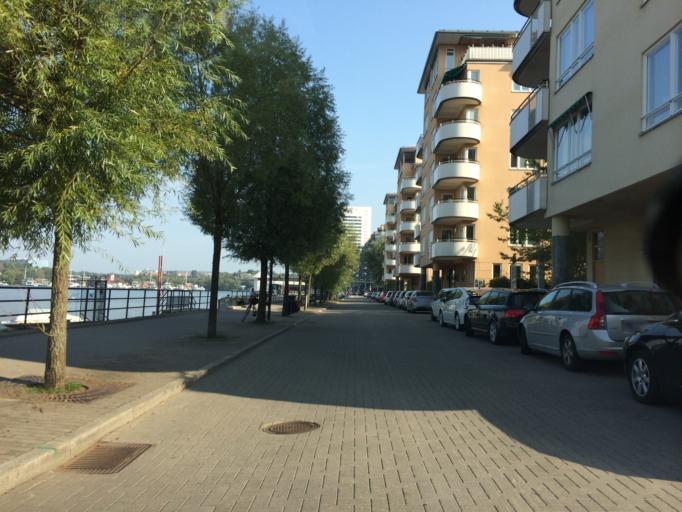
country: SE
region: Stockholm
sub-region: Solna Kommun
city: Solna
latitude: 59.3370
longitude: 17.9982
